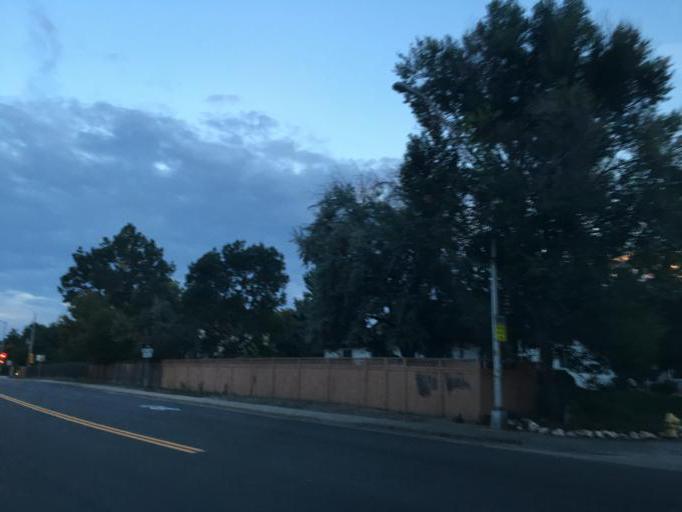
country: US
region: Colorado
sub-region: Adams County
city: Aurora
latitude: 39.6894
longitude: -104.8488
